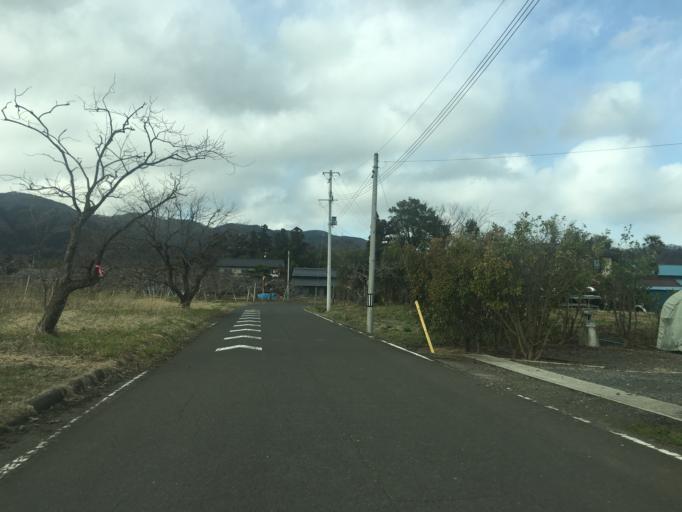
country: JP
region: Fukushima
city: Yanagawamachi-saiwaicho
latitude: 37.8865
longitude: 140.5818
